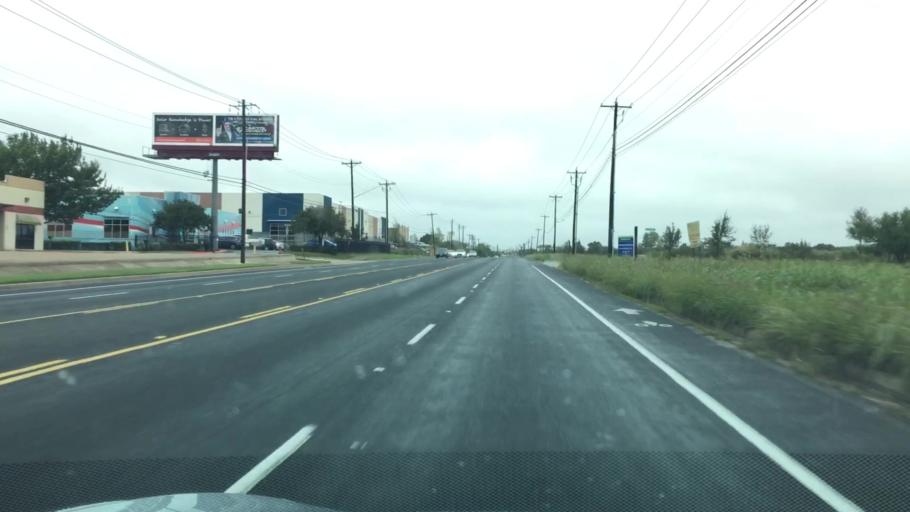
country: US
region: Texas
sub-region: Travis County
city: Austin
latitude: 30.1941
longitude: -97.7007
